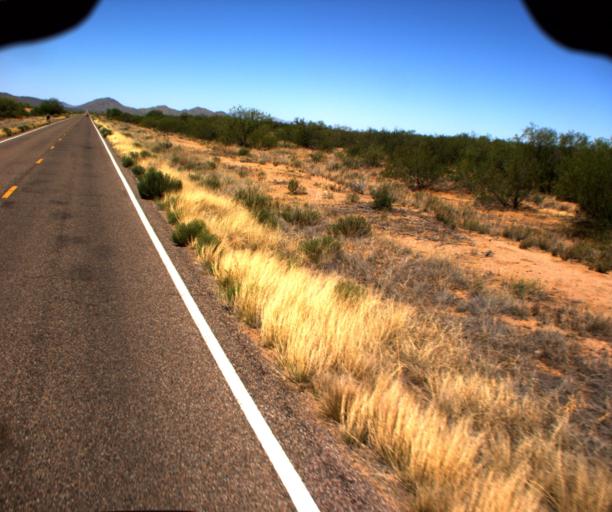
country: US
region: Arizona
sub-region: Yavapai County
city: Congress
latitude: 34.1391
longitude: -112.9111
